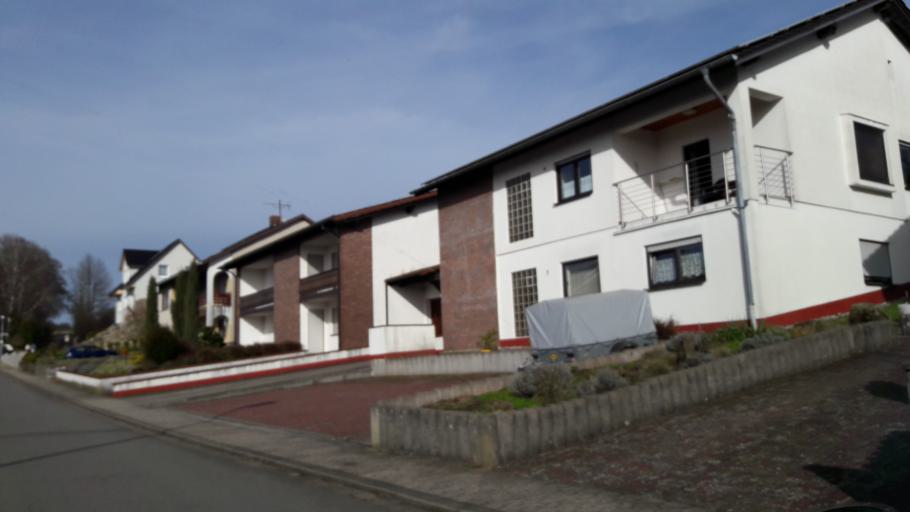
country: DE
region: Rheinland-Pfalz
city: Zweibrucken
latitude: 49.2714
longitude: 7.3235
